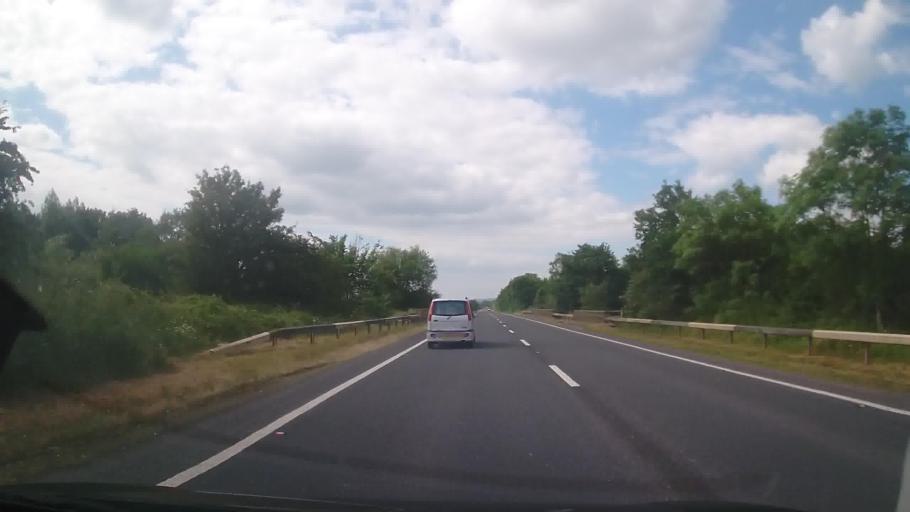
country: GB
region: England
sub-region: Herefordshire
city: Hope under Dinmore
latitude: 52.2070
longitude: -2.7220
